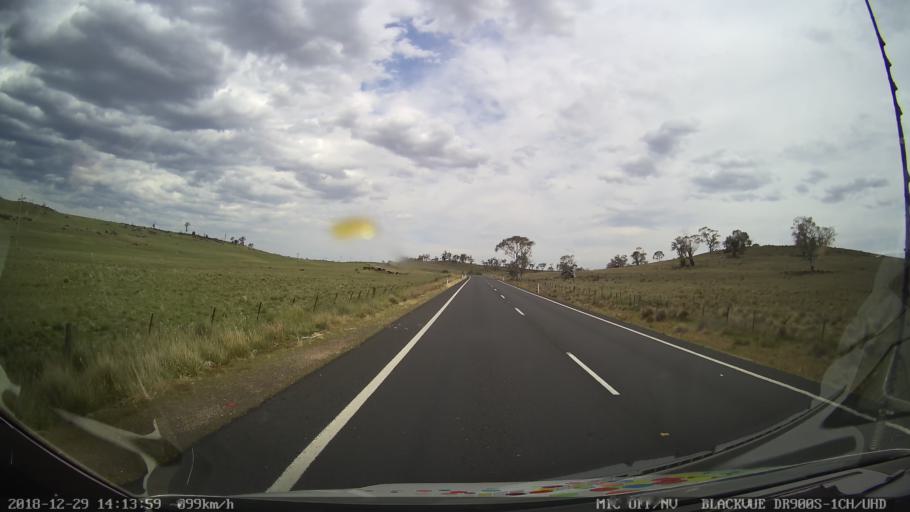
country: AU
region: New South Wales
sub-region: Cooma-Monaro
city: Cooma
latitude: -36.4361
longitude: 149.2378
